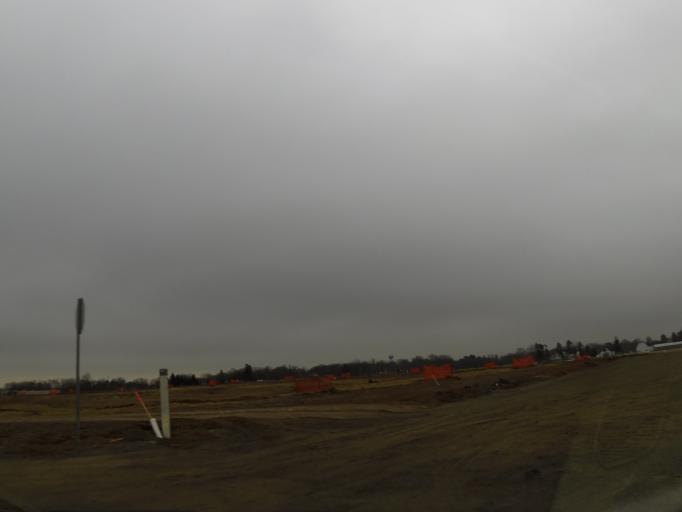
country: US
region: Minnesota
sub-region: Washington County
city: Lake Elmo
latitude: 45.0054
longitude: -92.8858
